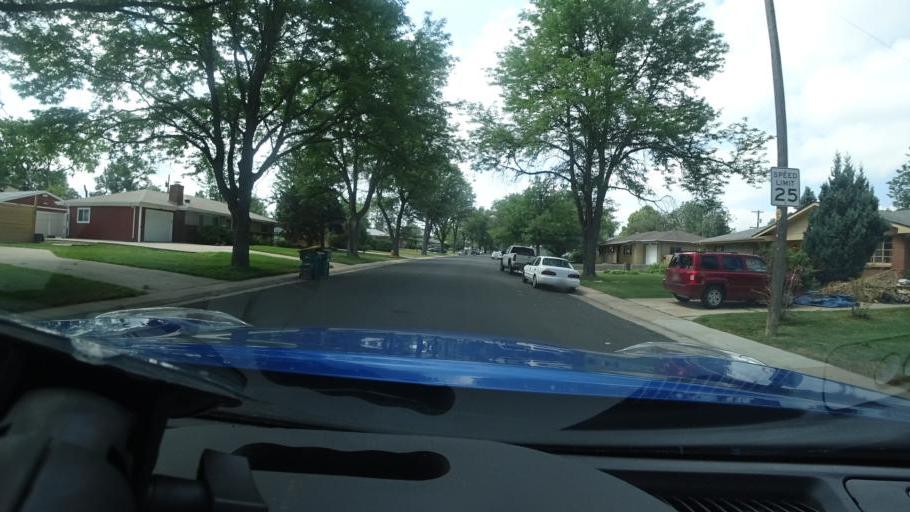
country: US
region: Colorado
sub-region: Adams County
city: Aurora
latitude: 39.7211
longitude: -104.8587
